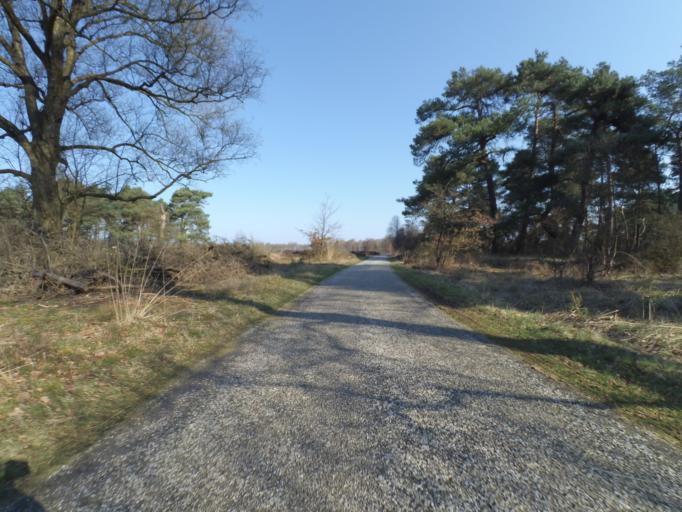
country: NL
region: Gelderland
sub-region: Gemeente Arnhem
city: Hoogkamp
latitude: 52.0553
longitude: 5.8512
